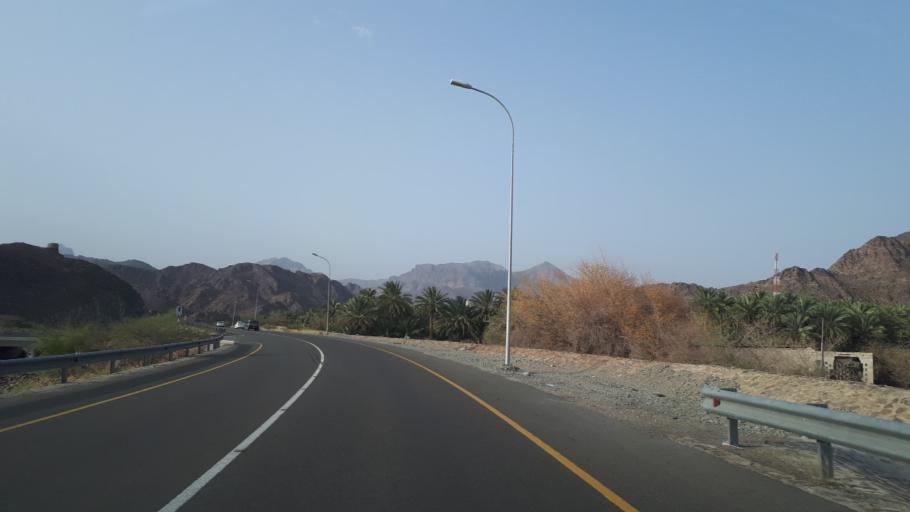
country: OM
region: Az Zahirah
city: Yanqul
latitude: 23.4913
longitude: 56.8277
